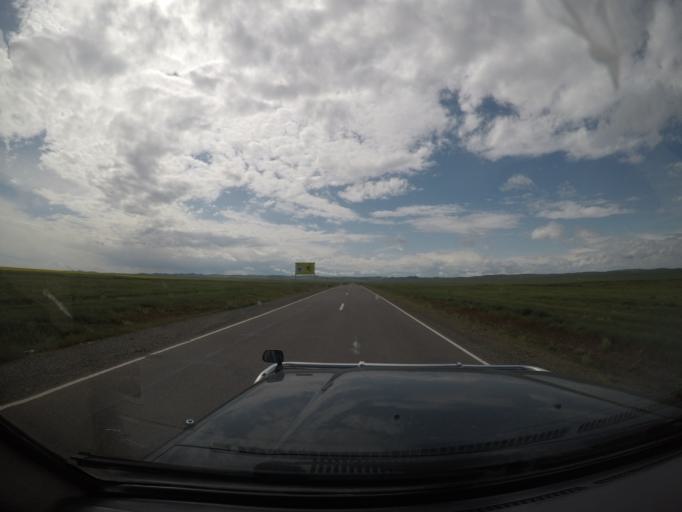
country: MN
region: Hentiy
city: Moron
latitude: 47.4183
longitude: 109.9349
